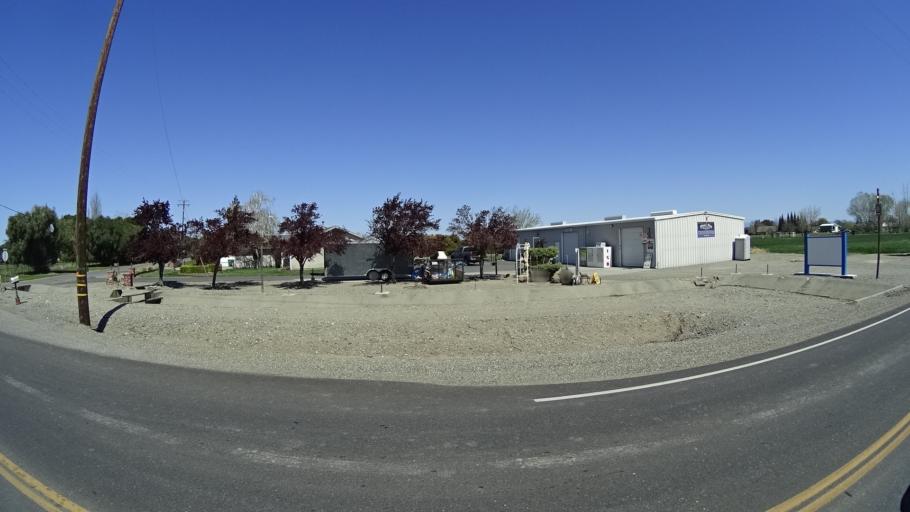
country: US
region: California
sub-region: Glenn County
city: Orland
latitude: 39.7636
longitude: -122.2387
